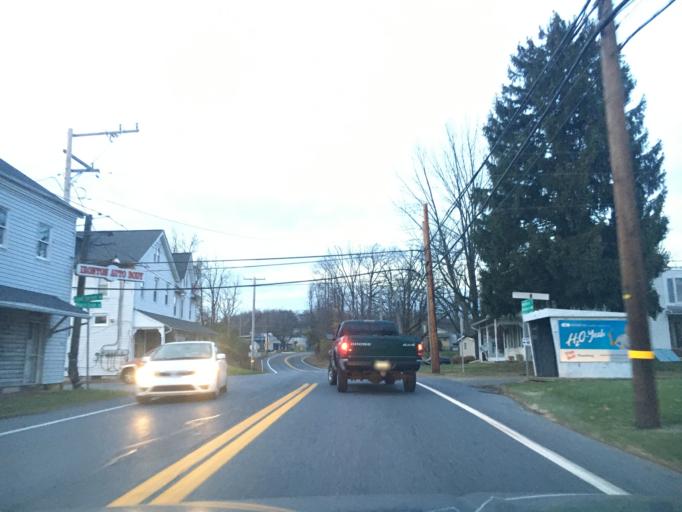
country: US
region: Pennsylvania
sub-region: Lehigh County
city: Egypt
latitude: 40.6700
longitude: -75.5673
